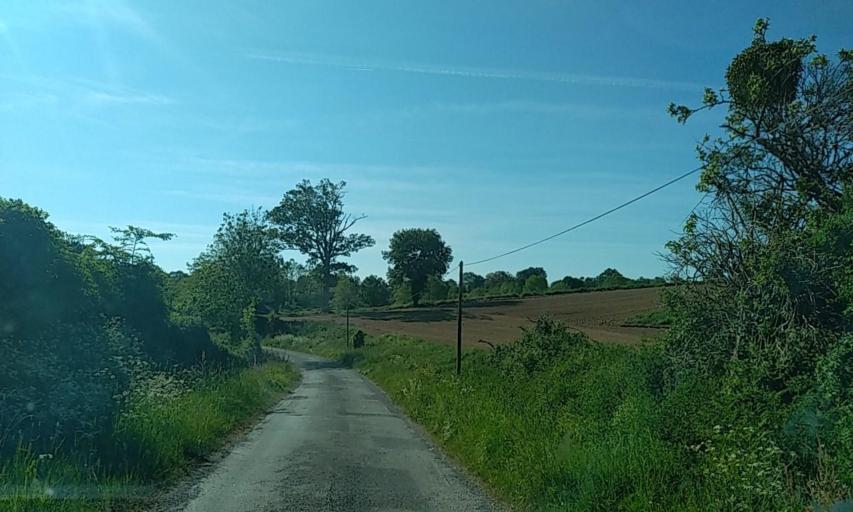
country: FR
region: Poitou-Charentes
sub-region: Departement des Deux-Sevres
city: Boisme
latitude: 46.7819
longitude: -0.4343
